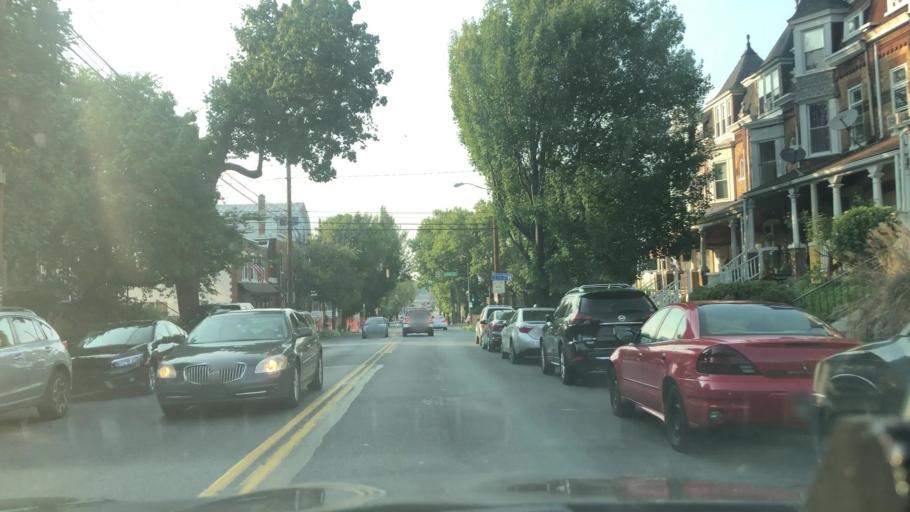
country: US
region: Pennsylvania
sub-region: Lehigh County
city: Allentown
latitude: 40.6011
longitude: -75.4896
